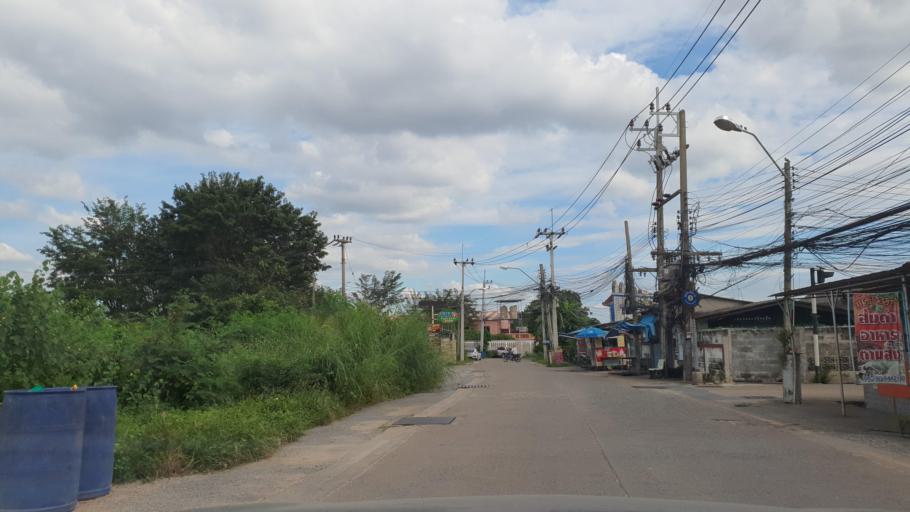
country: TH
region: Chon Buri
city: Phatthaya
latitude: 12.9582
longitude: 100.9107
